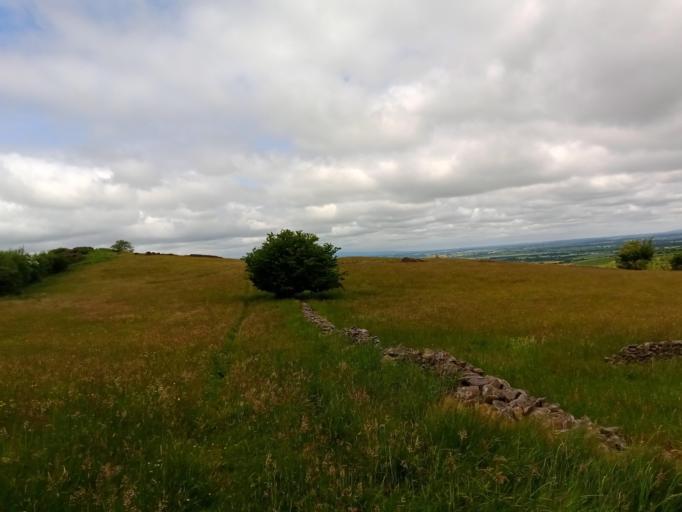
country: IE
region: Leinster
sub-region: Laois
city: Rathdowney
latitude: 52.7975
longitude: -7.4668
